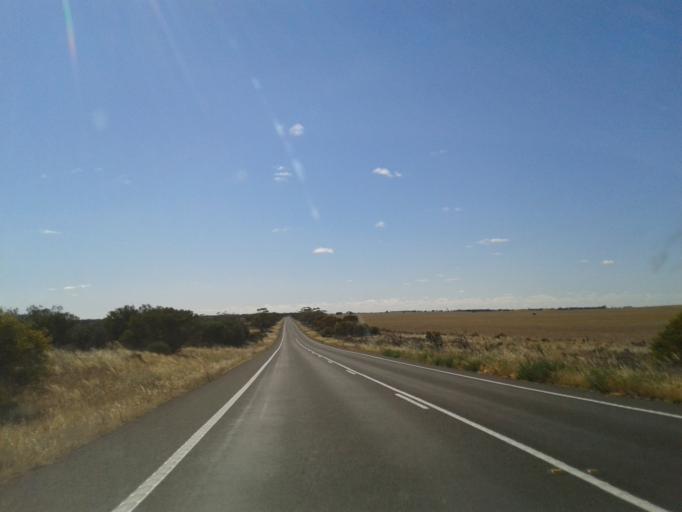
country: AU
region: South Australia
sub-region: Renmark Paringa
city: Renmark
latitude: -34.2748
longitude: 141.2698
